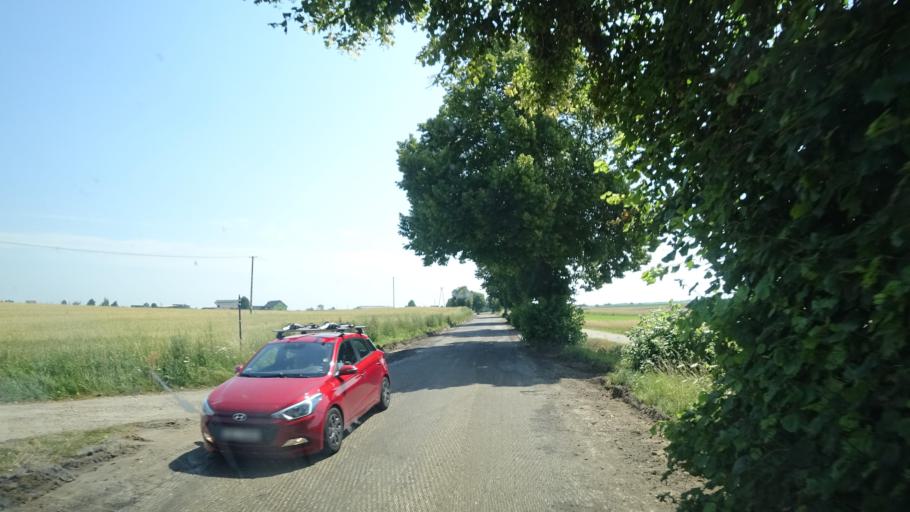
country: PL
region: Pomeranian Voivodeship
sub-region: Powiat chojnicki
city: Brusy
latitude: 53.8733
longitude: 17.6626
